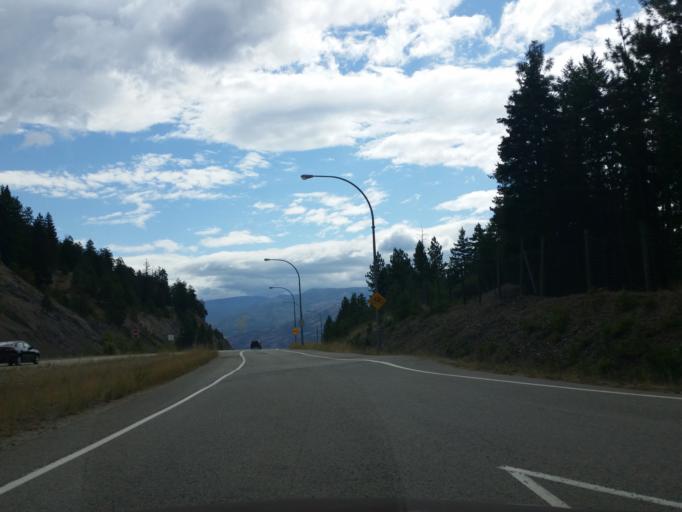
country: CA
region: British Columbia
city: Peachland
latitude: 49.8036
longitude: -119.7112
